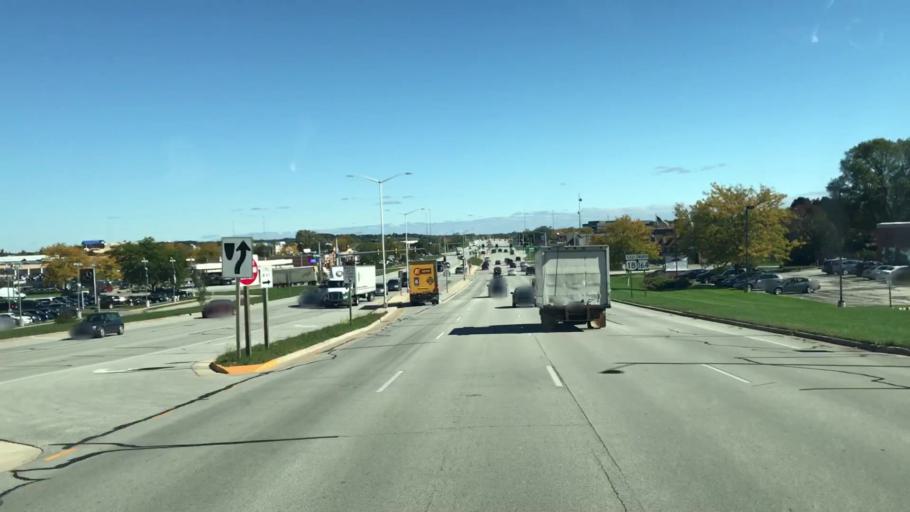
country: US
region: Wisconsin
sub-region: Waukesha County
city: Waukesha
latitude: 43.0295
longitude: -88.1830
